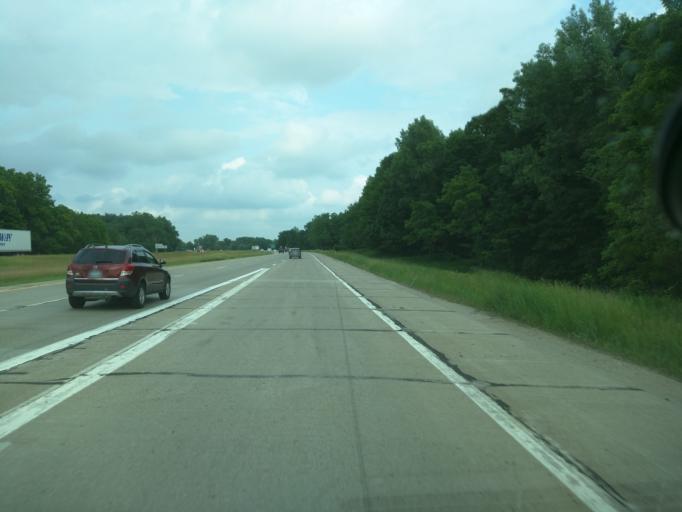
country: US
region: Michigan
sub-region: Clinton County
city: DeWitt
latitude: 42.8074
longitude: -84.5958
